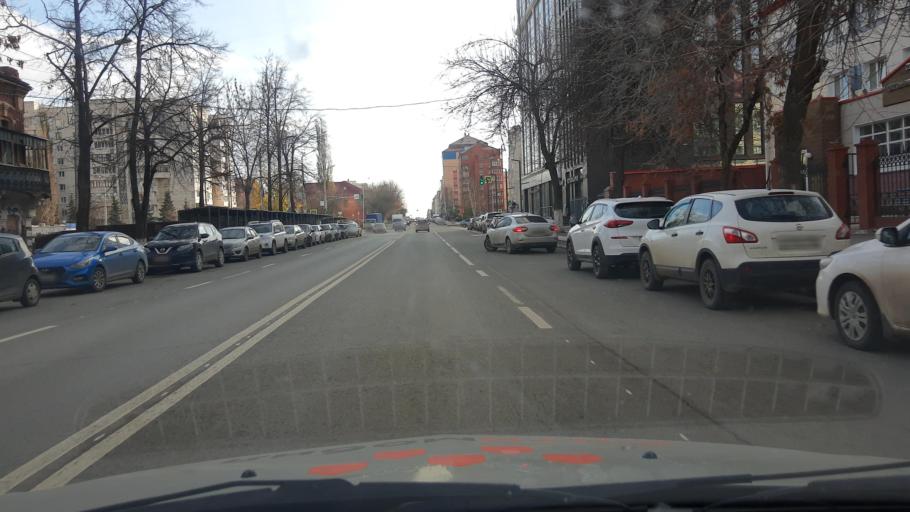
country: RU
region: Bashkortostan
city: Ufa
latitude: 54.7308
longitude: 55.9347
